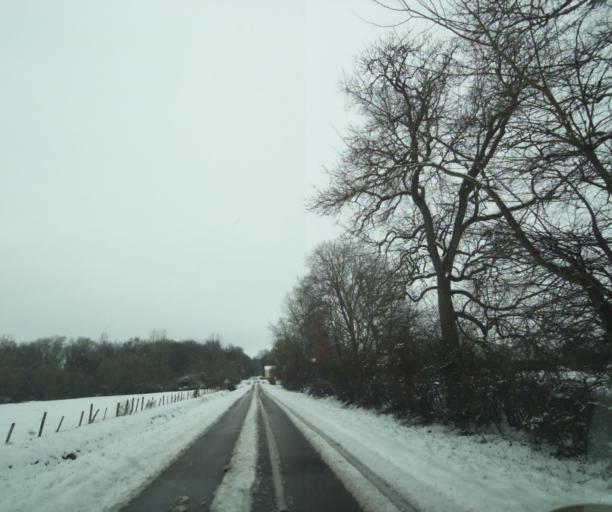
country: FR
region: Champagne-Ardenne
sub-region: Departement de la Haute-Marne
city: Montier-en-Der
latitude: 48.4699
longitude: 4.6591
